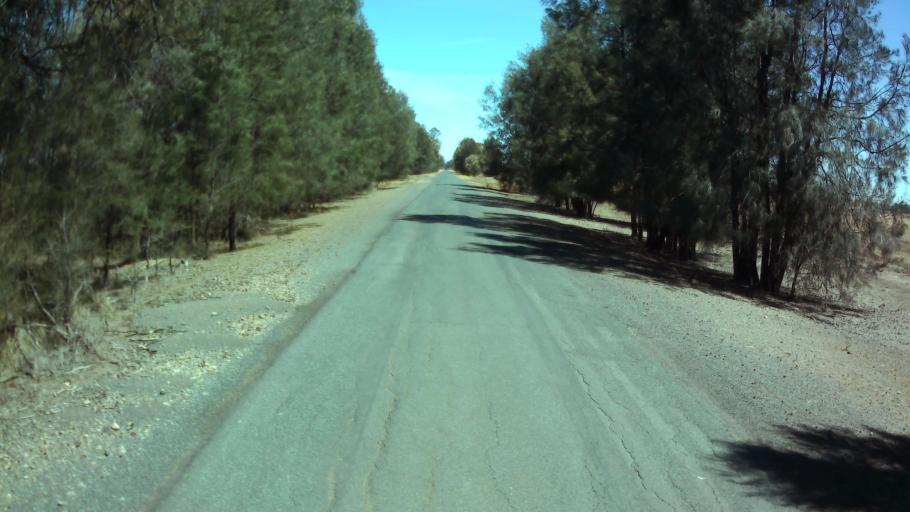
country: AU
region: New South Wales
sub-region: Weddin
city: Grenfell
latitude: -33.8858
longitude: 147.6892
